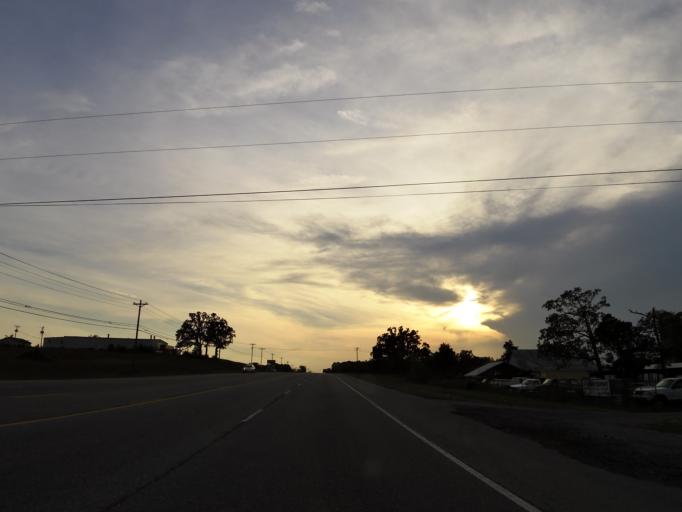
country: US
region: Tennessee
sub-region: Loudon County
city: Greenback
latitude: 35.6509
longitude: -84.1313
